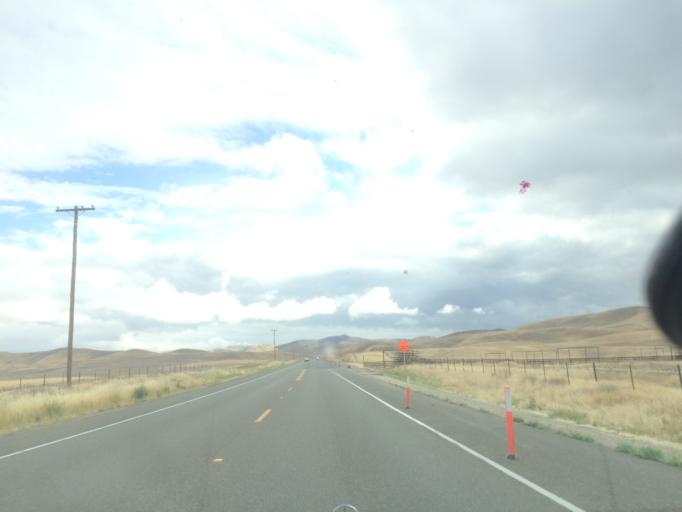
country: US
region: California
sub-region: San Luis Obispo County
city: Shandon
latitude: 35.7425
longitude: -120.2761
